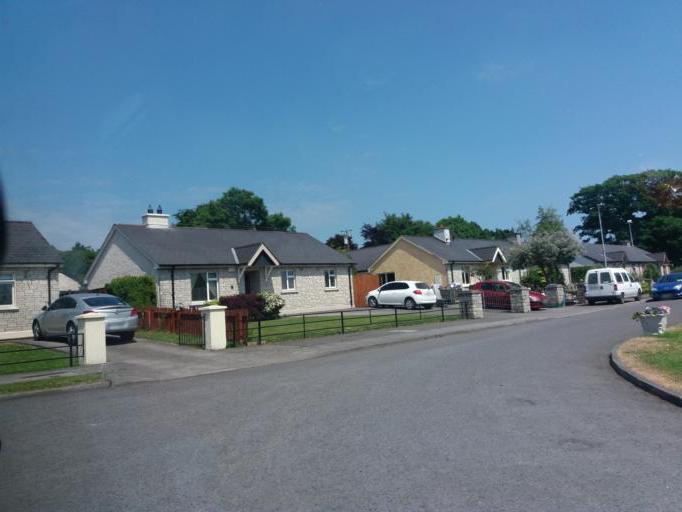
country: IE
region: Leinster
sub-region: An Mhi
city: Slane
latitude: 53.7126
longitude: -6.5423
